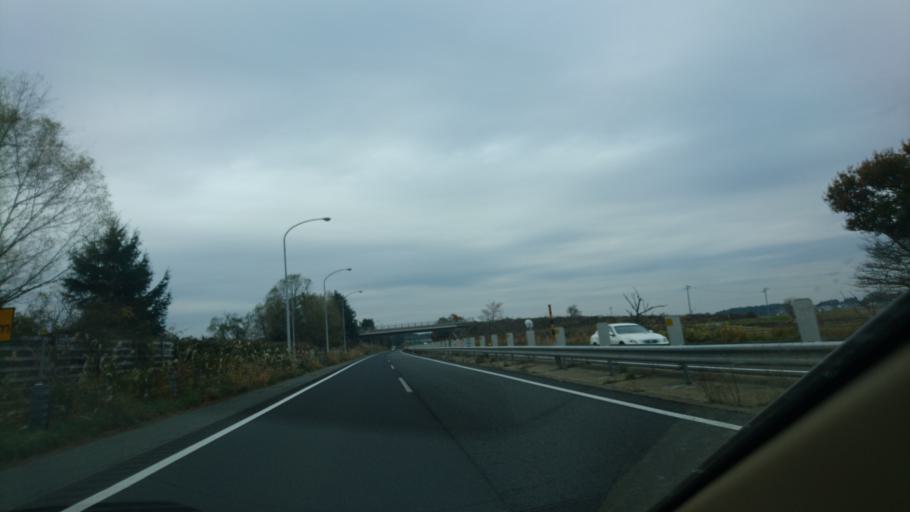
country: JP
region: Iwate
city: Kitakami
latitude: 39.2572
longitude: 141.0771
